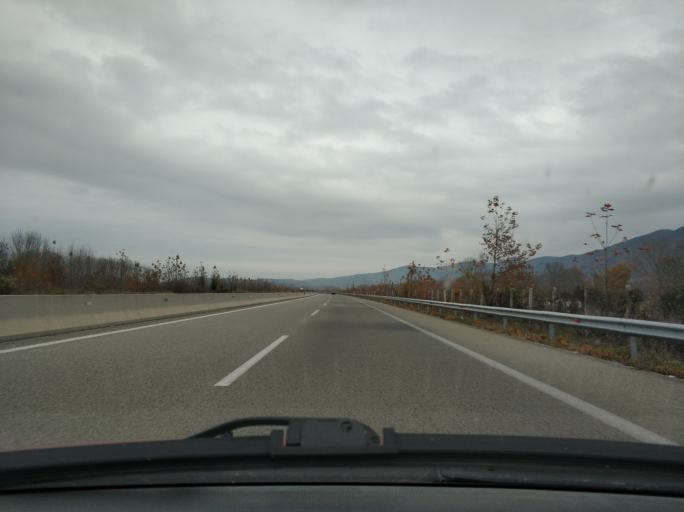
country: GR
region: East Macedonia and Thrace
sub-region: Nomos Kavalas
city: Eleftheres
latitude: 40.8693
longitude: 24.1977
